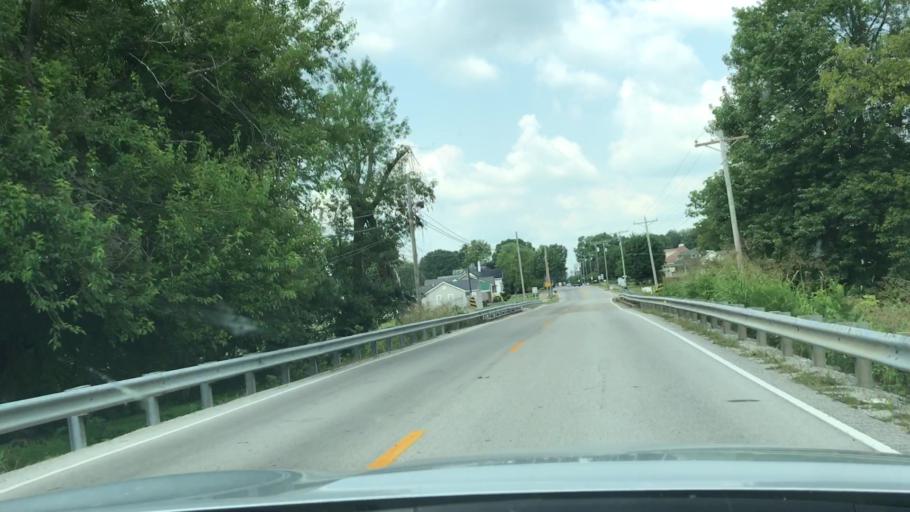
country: US
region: Kentucky
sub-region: Todd County
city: Elkton
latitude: 36.8082
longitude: -87.1450
